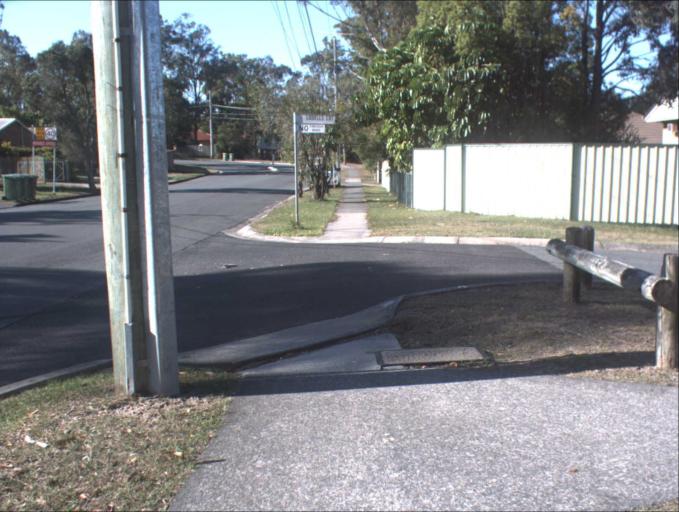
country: AU
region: Queensland
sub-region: Logan
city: Logan City
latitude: -27.6562
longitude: 153.1058
